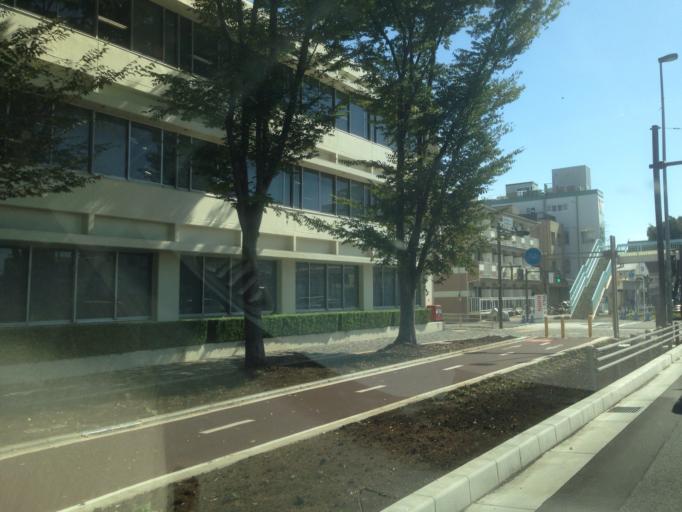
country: JP
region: Tokyo
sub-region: Machida-shi
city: Machida
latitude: 35.5711
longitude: 139.3781
